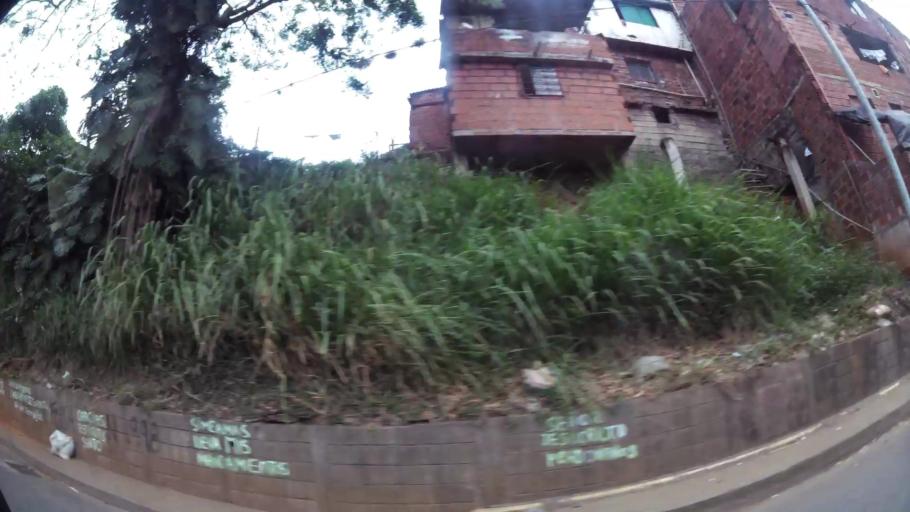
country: CO
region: Antioquia
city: Bello
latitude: 6.2990
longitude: -75.5577
